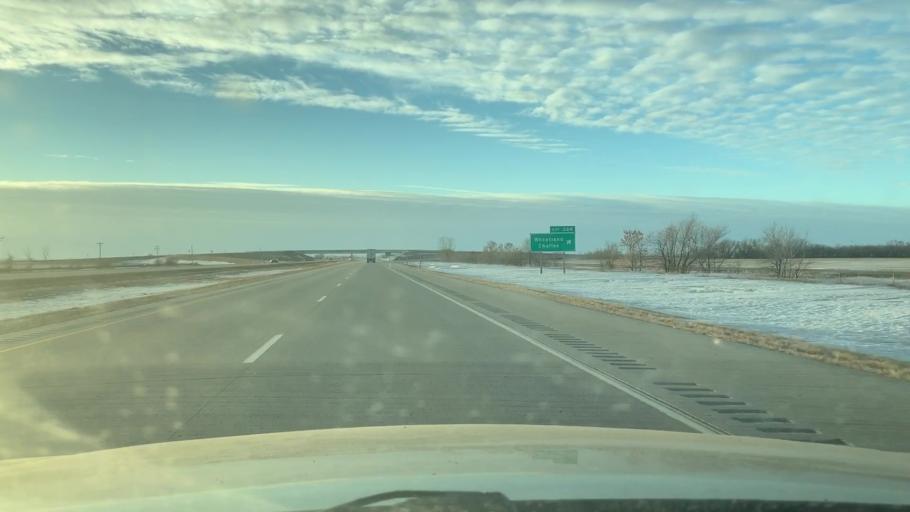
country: US
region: North Dakota
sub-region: Cass County
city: Casselton
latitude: 46.8760
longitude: -97.3373
